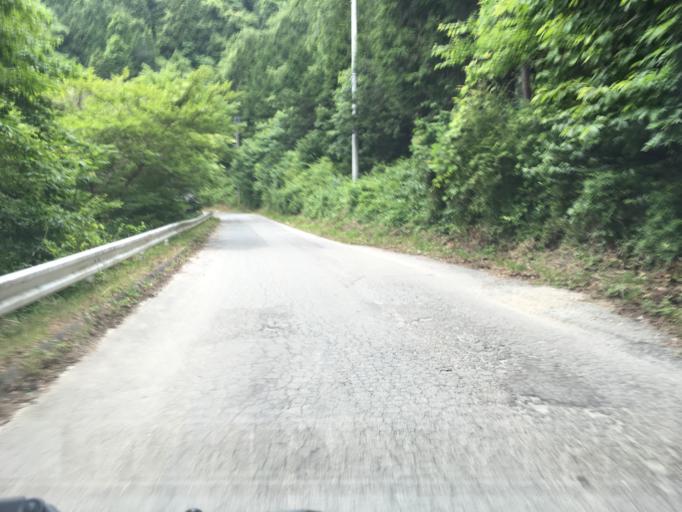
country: JP
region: Miyagi
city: Marumori
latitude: 37.7909
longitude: 140.7840
